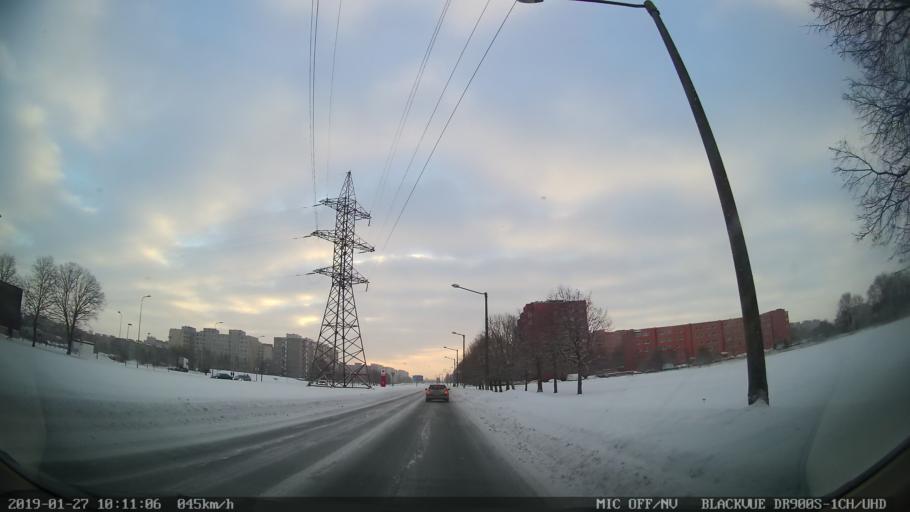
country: EE
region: Harju
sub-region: Viimsi vald
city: Viimsi
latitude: 59.4431
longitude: 24.8216
